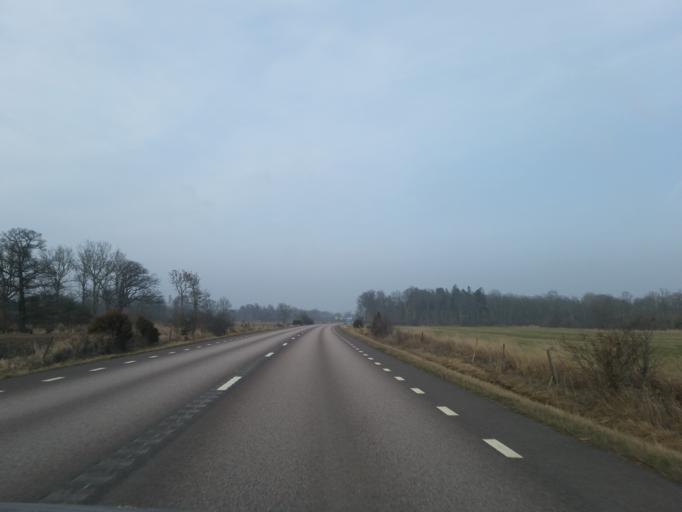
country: SE
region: Kalmar
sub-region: Borgholms Kommun
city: Borgholm
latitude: 57.1029
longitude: 16.9366
